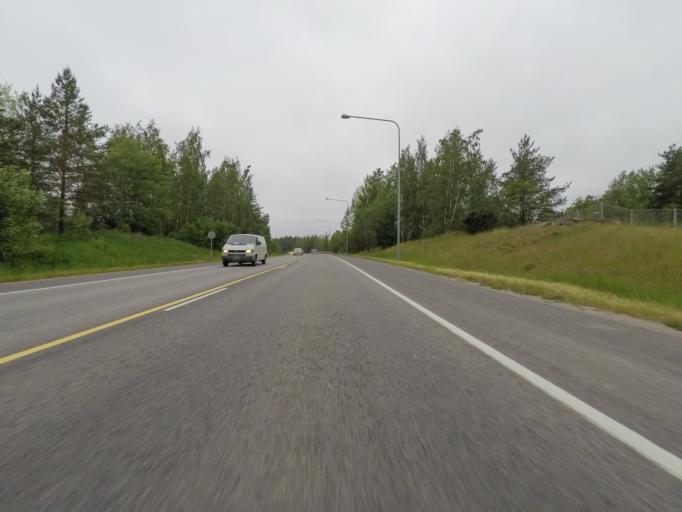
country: FI
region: Varsinais-Suomi
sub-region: Turku
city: Raisio
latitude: 60.4611
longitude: 22.1759
